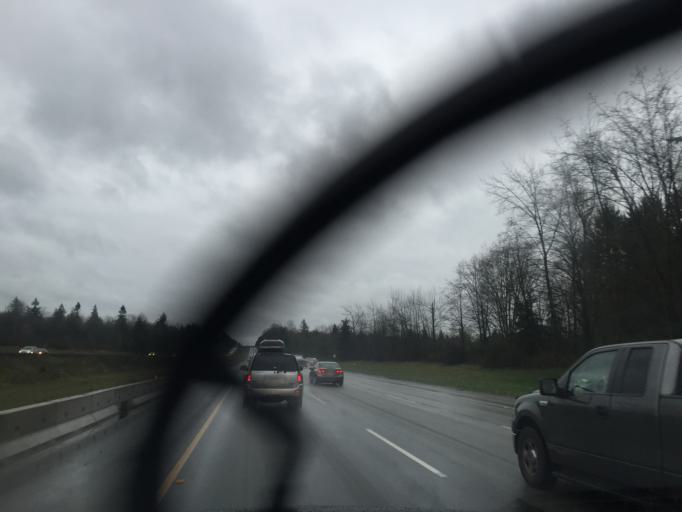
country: CA
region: British Columbia
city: Langley
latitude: 49.1253
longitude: -122.5536
